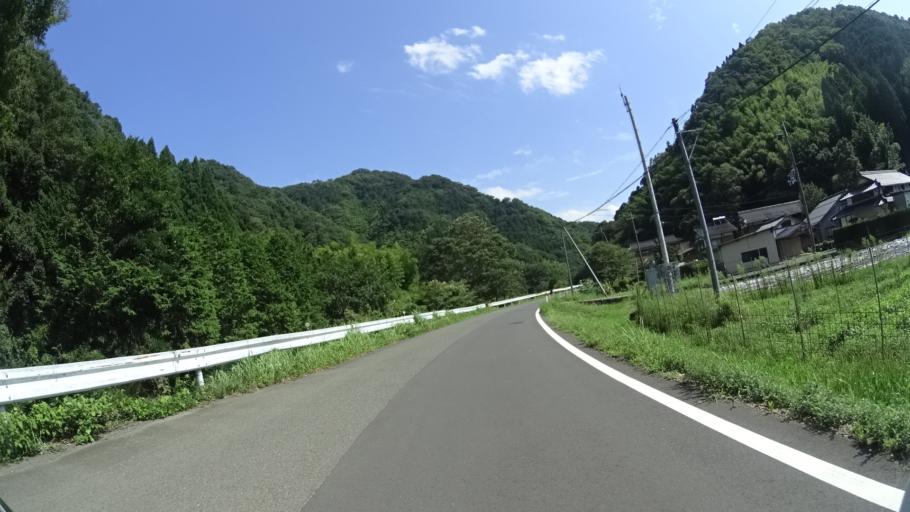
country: JP
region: Kyoto
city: Maizuru
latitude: 35.4276
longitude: 135.2970
